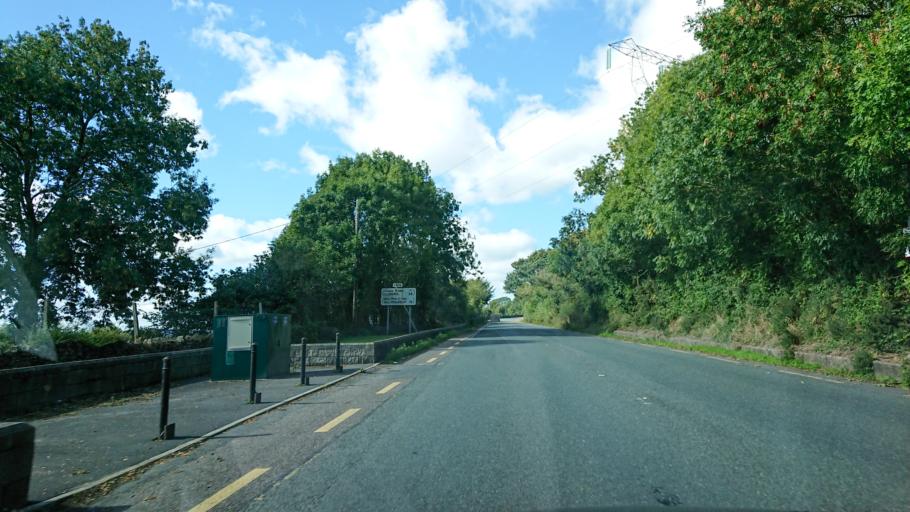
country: IE
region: Munster
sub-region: Waterford
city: Dungarvan
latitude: 52.1100
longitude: -7.6749
